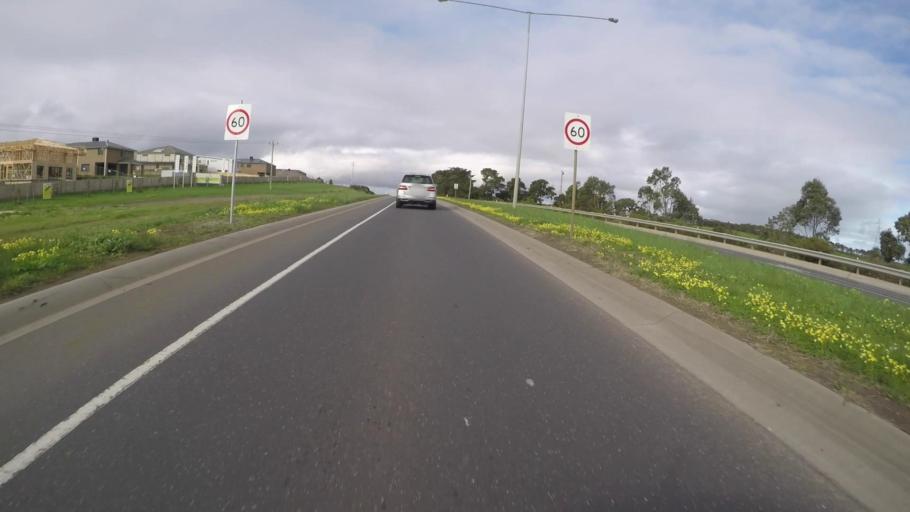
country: AU
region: Victoria
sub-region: Greater Geelong
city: Wandana Heights
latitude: -38.1720
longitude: 144.2939
